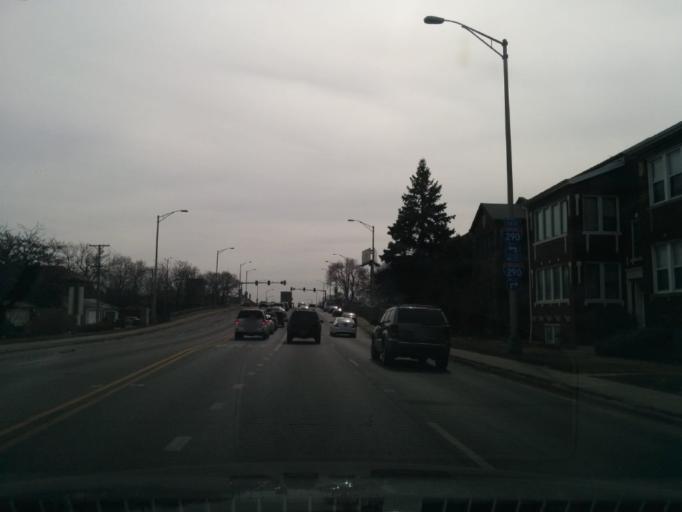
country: US
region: Illinois
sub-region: Cook County
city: Forest Park
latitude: 41.8753
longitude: -87.8046
